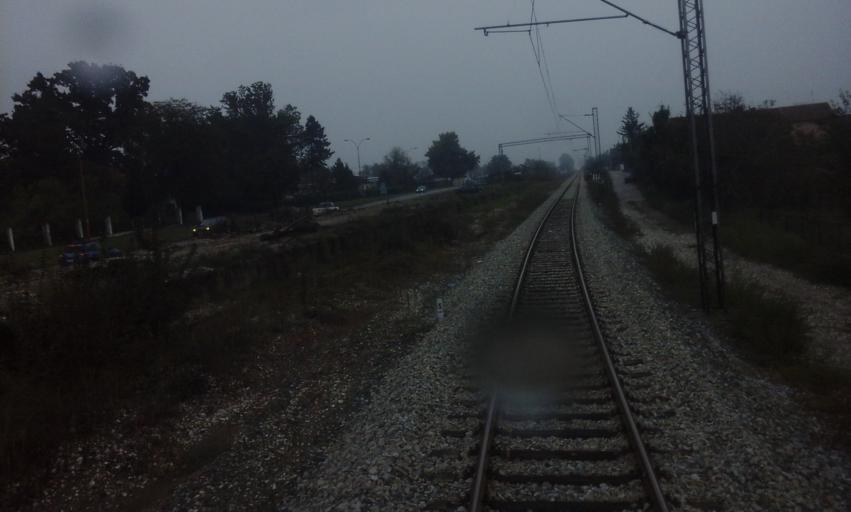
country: RS
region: Central Serbia
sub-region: Pomoravski Okrug
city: Cuprija
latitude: 43.9144
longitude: 21.3756
